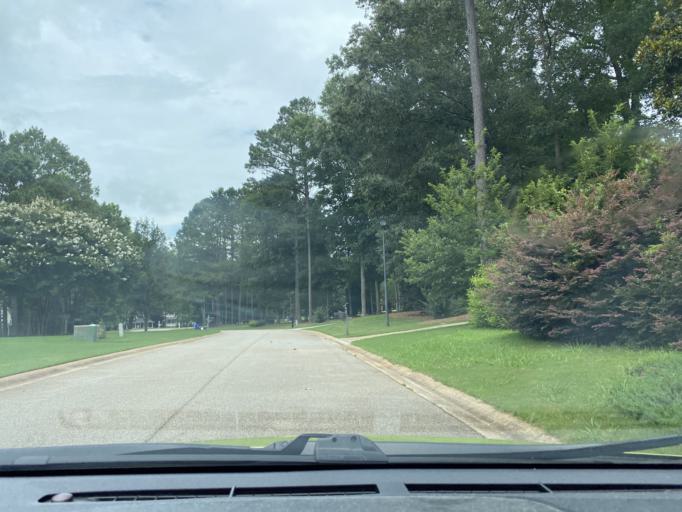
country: US
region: Georgia
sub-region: Fayette County
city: Peachtree City
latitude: 33.4260
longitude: -84.6749
